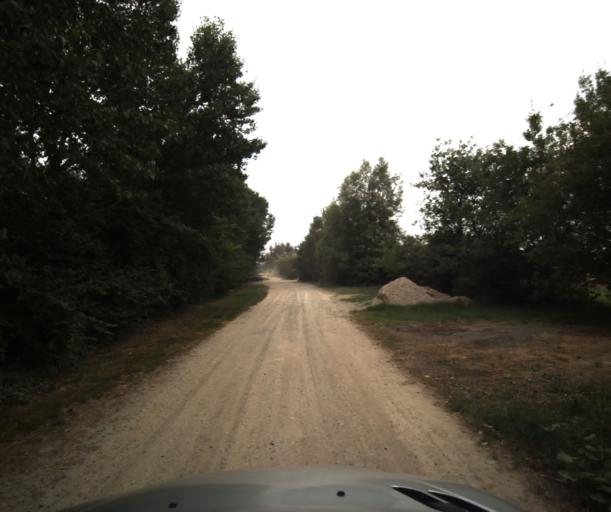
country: FR
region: Midi-Pyrenees
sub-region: Departement de la Haute-Garonne
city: Vieille-Toulouse
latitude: 43.5385
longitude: 1.4248
